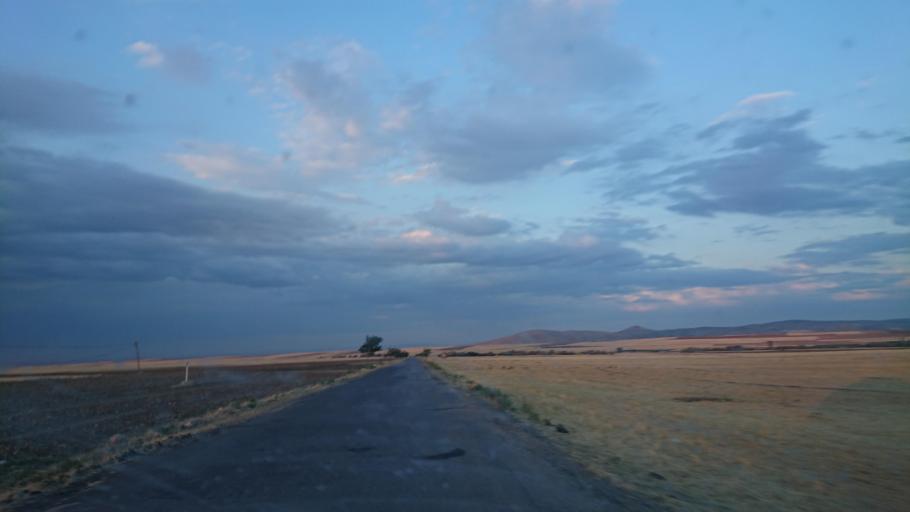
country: TR
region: Aksaray
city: Balci
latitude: 38.8245
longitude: 34.1085
